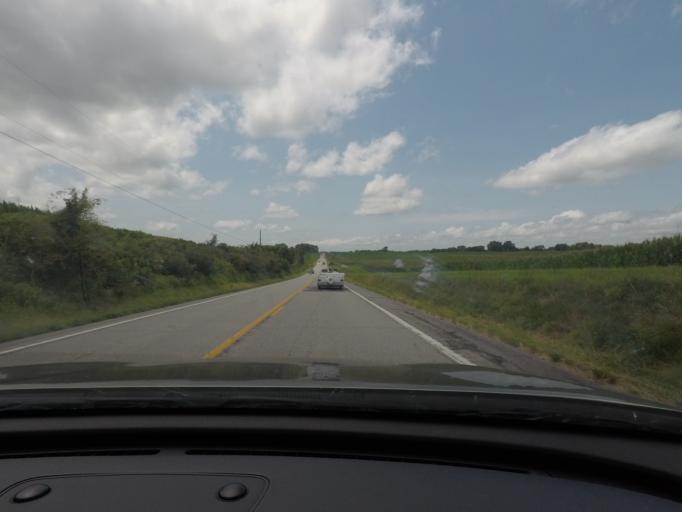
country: US
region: Missouri
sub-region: Carroll County
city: Carrollton
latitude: 39.2026
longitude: -93.4596
